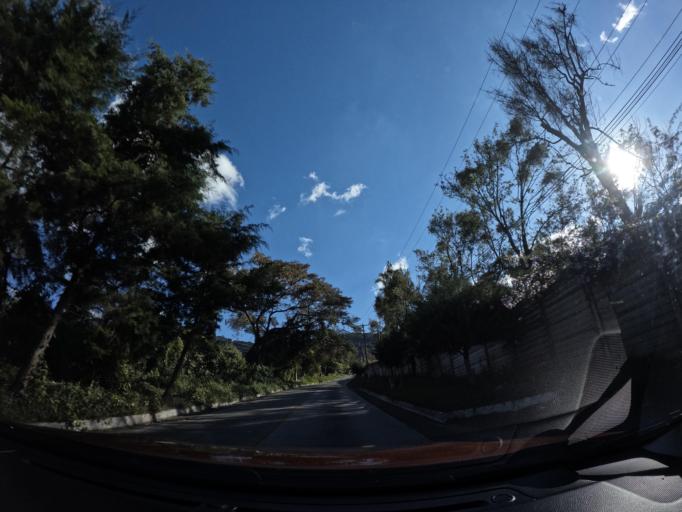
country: GT
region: Sacatepequez
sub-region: Municipio de Santa Maria de Jesus
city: Santa Maria de Jesus
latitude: 14.5192
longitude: -90.7226
